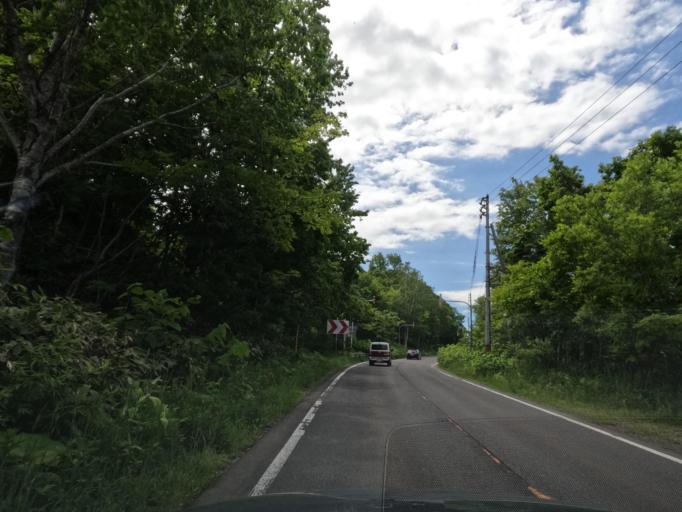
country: JP
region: Hokkaido
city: Bibai
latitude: 43.2448
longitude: 141.8934
